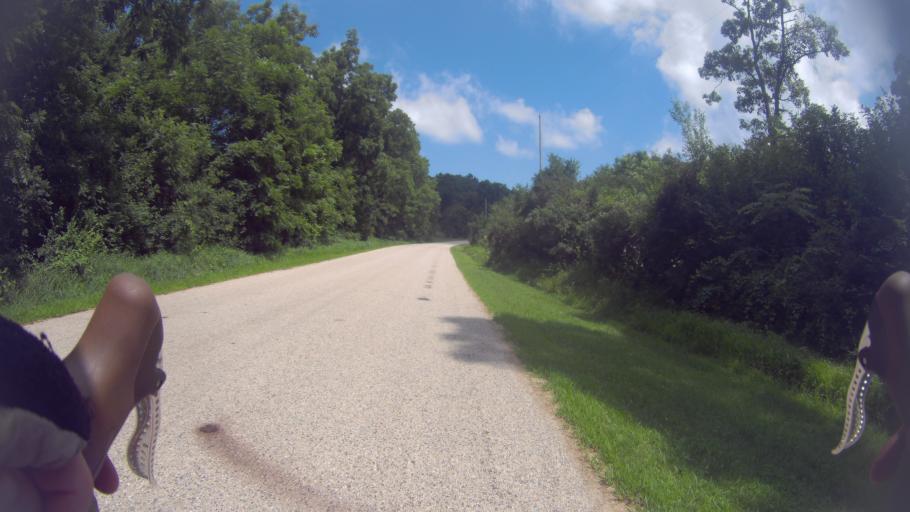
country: US
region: Wisconsin
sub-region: Sauk County
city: Sauk City
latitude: 43.2265
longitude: -89.6204
